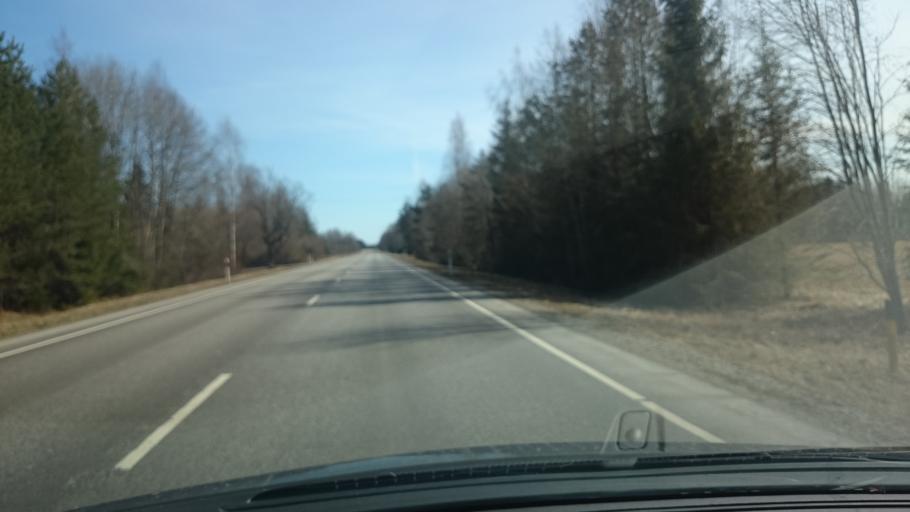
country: EE
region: Paernumaa
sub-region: Vaendra vald (alev)
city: Vandra
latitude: 58.6710
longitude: 25.1314
